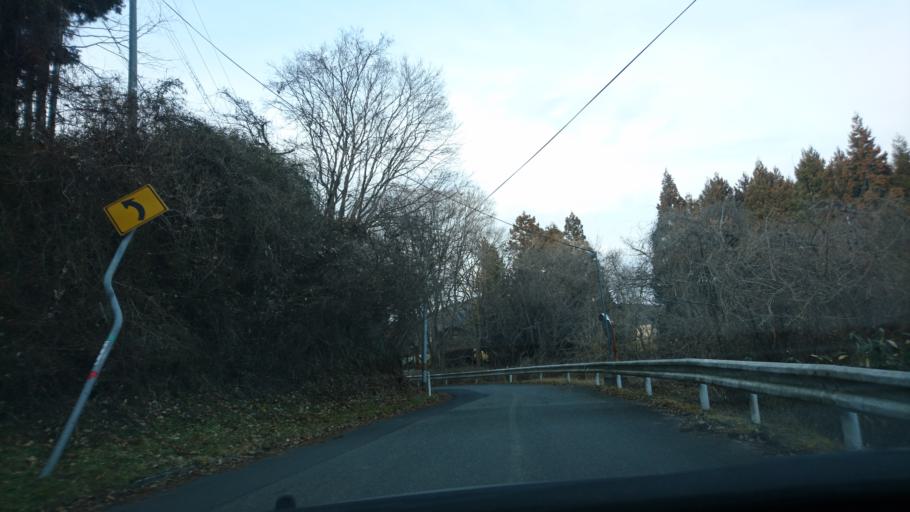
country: JP
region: Iwate
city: Ichinoseki
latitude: 38.8269
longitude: 141.2494
